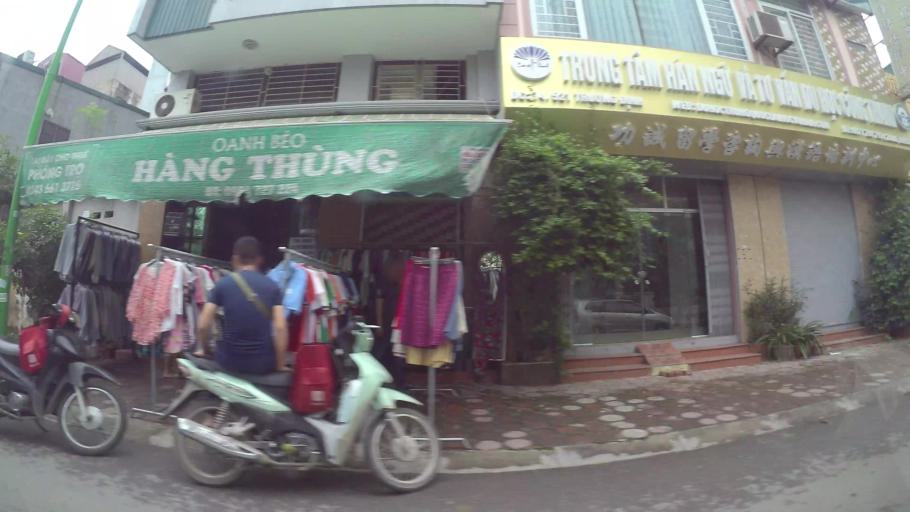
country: VN
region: Ha Noi
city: Hai BaTrung
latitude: 20.9805
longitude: 105.8459
